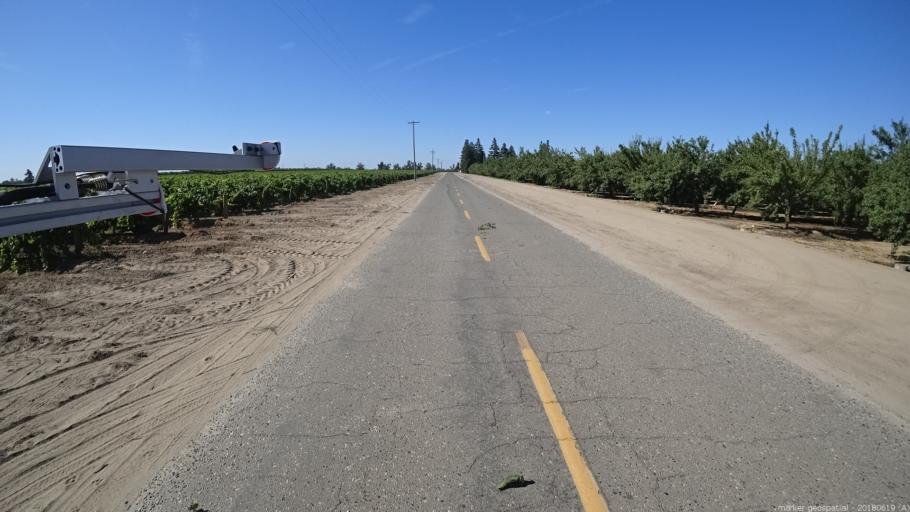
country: US
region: California
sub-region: Fresno County
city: Biola
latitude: 36.8331
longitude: -120.0788
